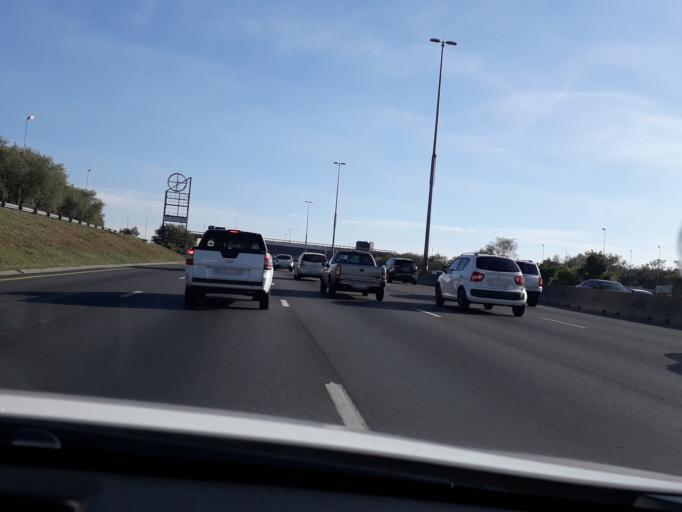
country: ZA
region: Gauteng
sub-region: City of Johannesburg Metropolitan Municipality
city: Midrand
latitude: -25.9830
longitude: 28.1253
